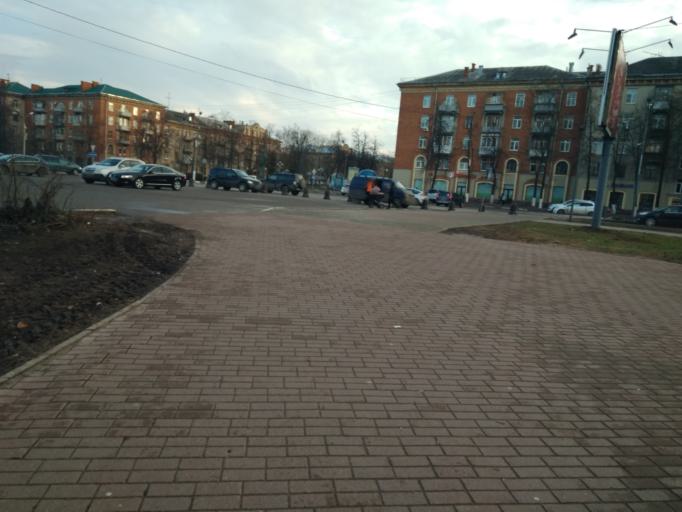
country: RU
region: Moskovskaya
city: Zhukovskiy
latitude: 55.5974
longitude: 38.1186
